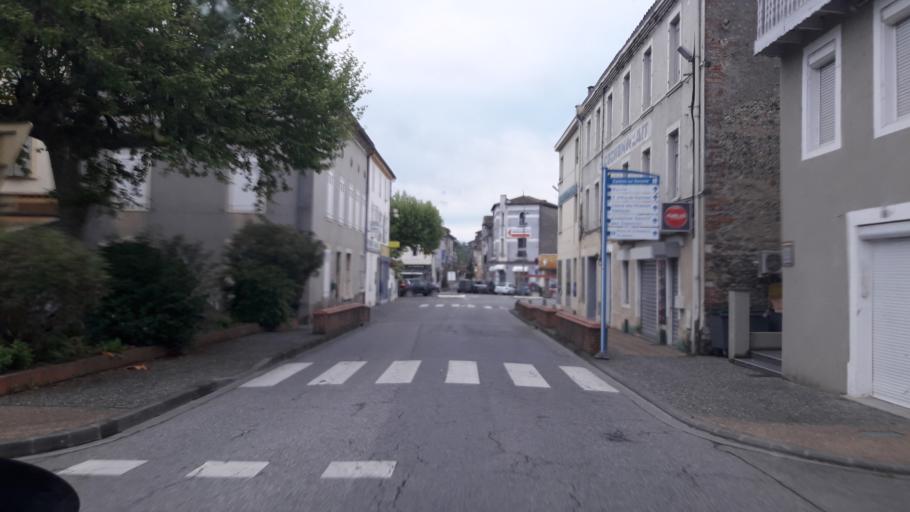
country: FR
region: Midi-Pyrenees
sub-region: Departement de la Haute-Garonne
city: Cazeres
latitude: 43.2079
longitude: 1.0859
